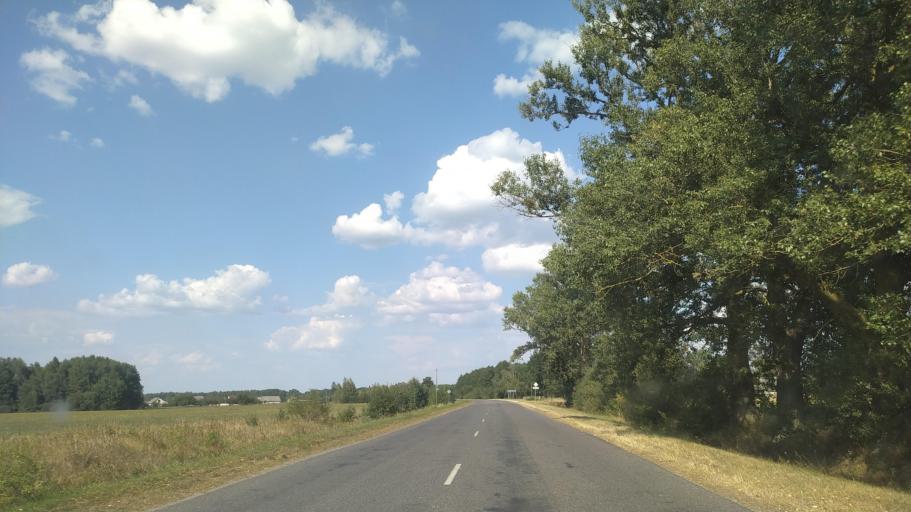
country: BY
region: Brest
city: Drahichyn
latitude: 52.1330
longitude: 25.1221
